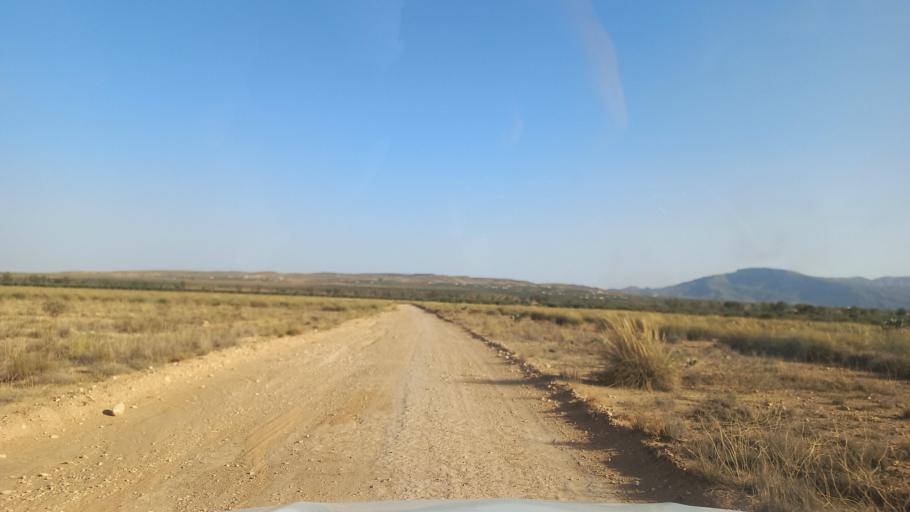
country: TN
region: Al Qasrayn
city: Kasserine
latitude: 35.2322
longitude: 8.9393
